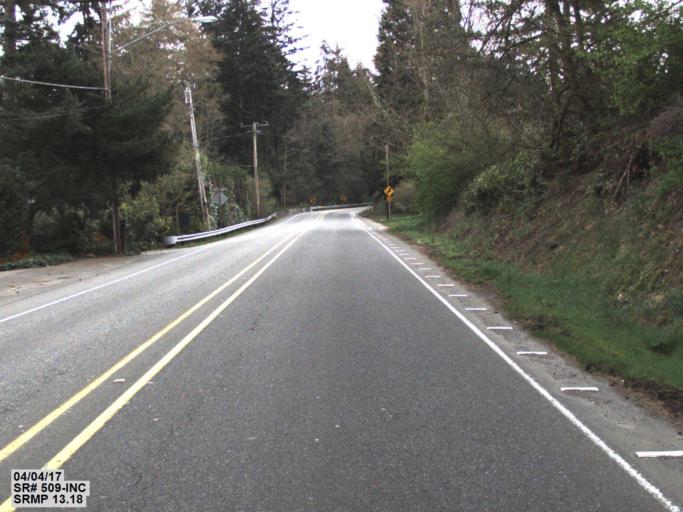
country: US
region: Washington
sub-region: King County
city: Federal Way
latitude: 47.3318
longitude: -122.3289
